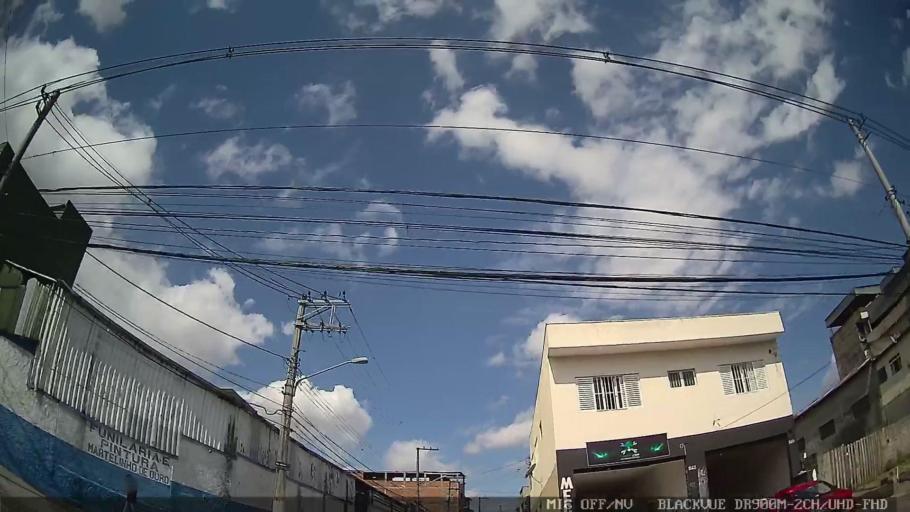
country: BR
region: Sao Paulo
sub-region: Guarulhos
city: Guarulhos
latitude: -23.4965
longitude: -46.4781
